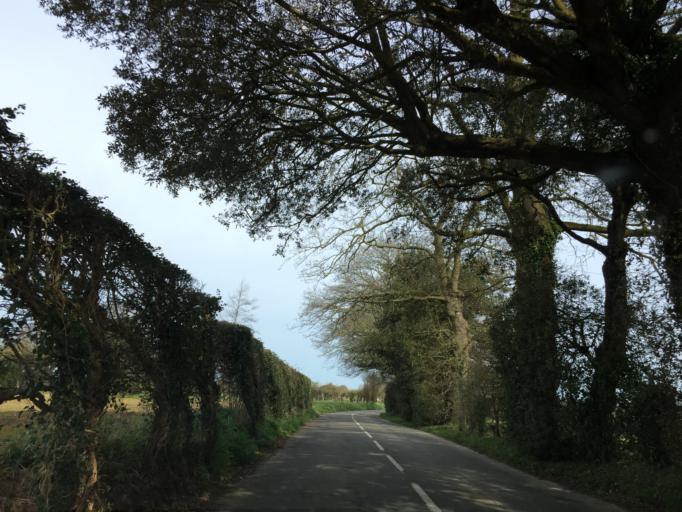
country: JE
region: St Helier
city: Saint Helier
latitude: 49.2209
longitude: -2.0579
